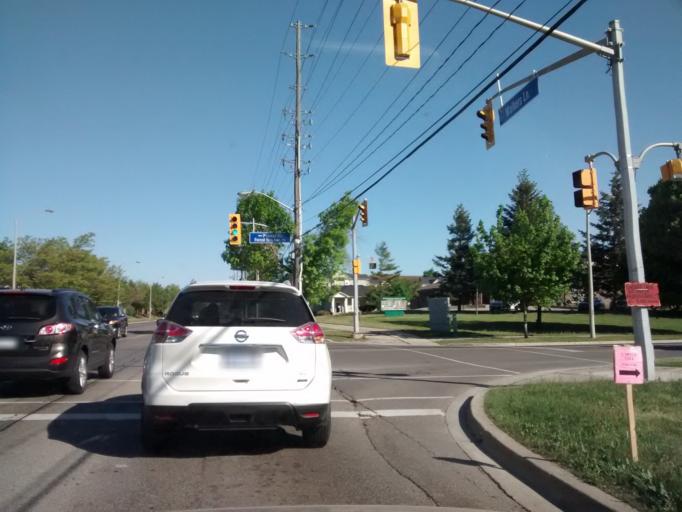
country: CA
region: Ontario
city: Burlington
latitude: 43.3752
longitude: -79.8002
